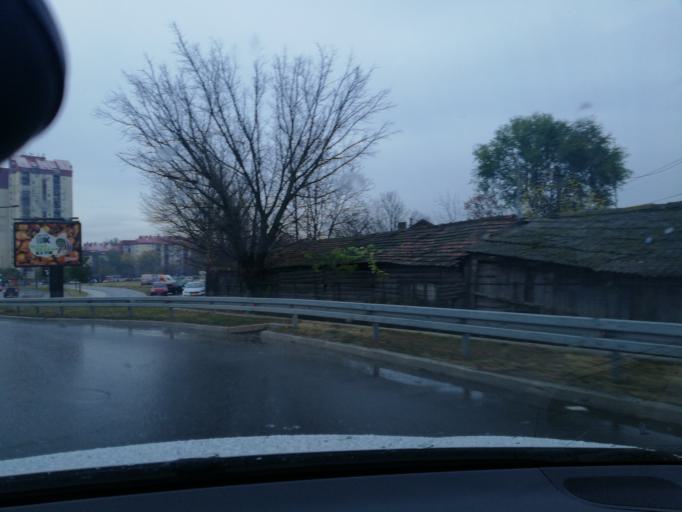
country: RS
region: Autonomna Pokrajina Vojvodina
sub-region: Juznobacki Okrug
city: Novi Sad
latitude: 45.2394
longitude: 19.8227
